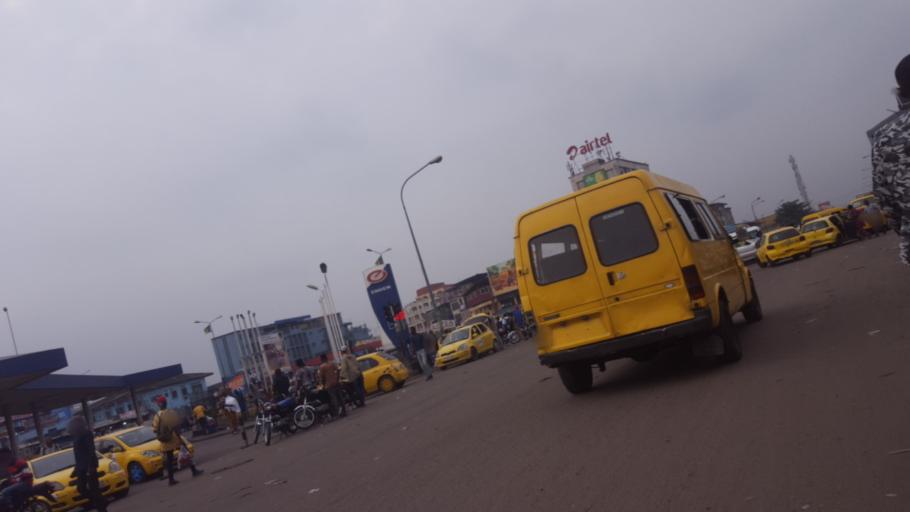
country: CD
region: Kinshasa
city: Kinshasa
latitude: -4.3402
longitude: 15.3138
